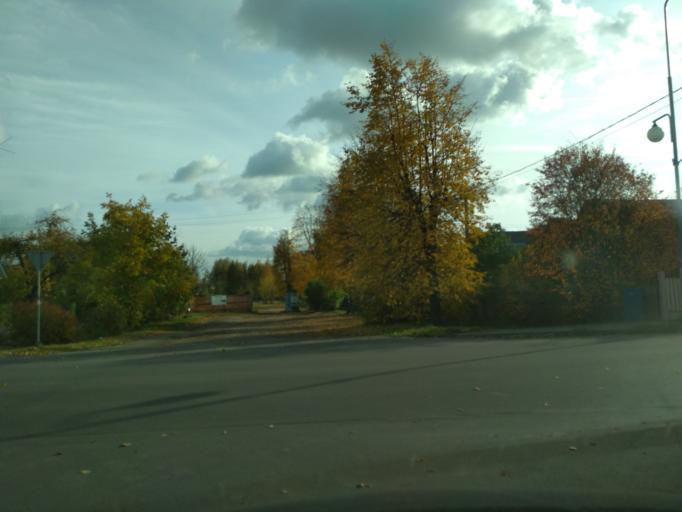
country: BY
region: Minsk
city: Mar''ina Horka
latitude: 53.5065
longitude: 28.1498
